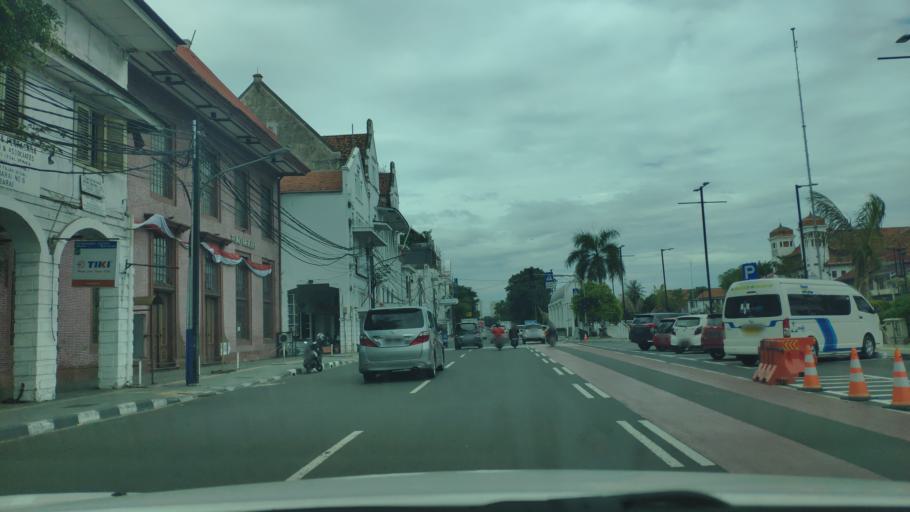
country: ID
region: Jakarta Raya
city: Jakarta
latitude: -6.1362
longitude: 106.8116
